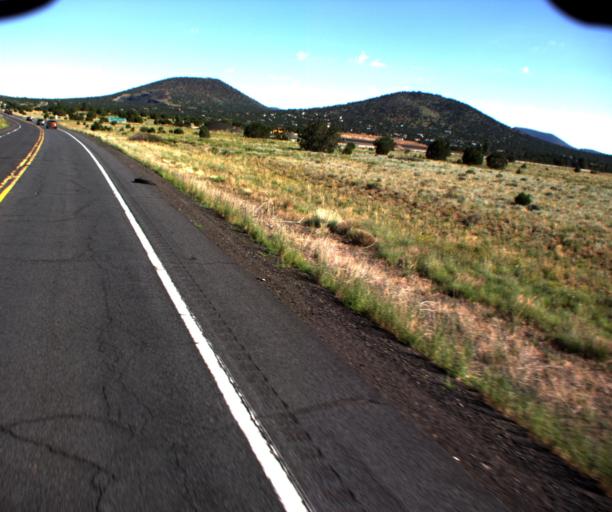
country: US
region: Arizona
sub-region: Coconino County
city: Williams
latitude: 35.3155
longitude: -112.1486
